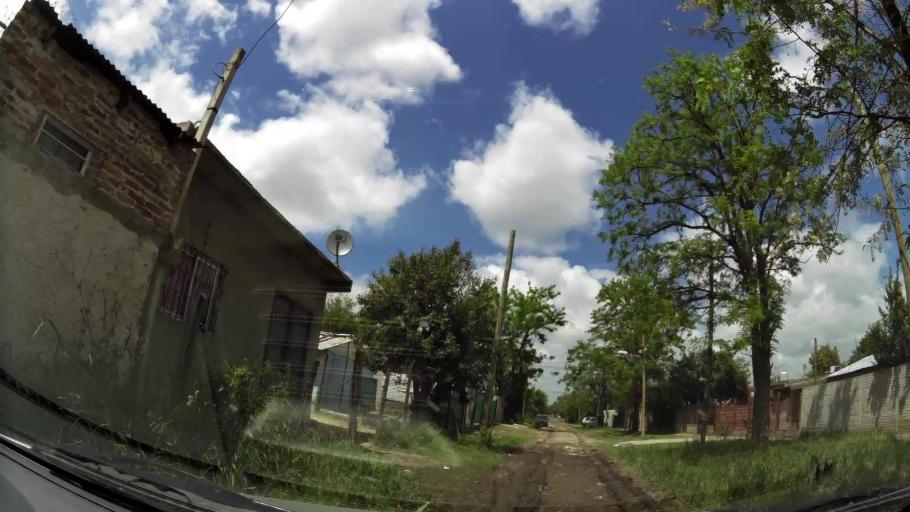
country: AR
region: Buenos Aires
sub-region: Partido de Quilmes
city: Quilmes
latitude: -34.8188
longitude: -58.2452
